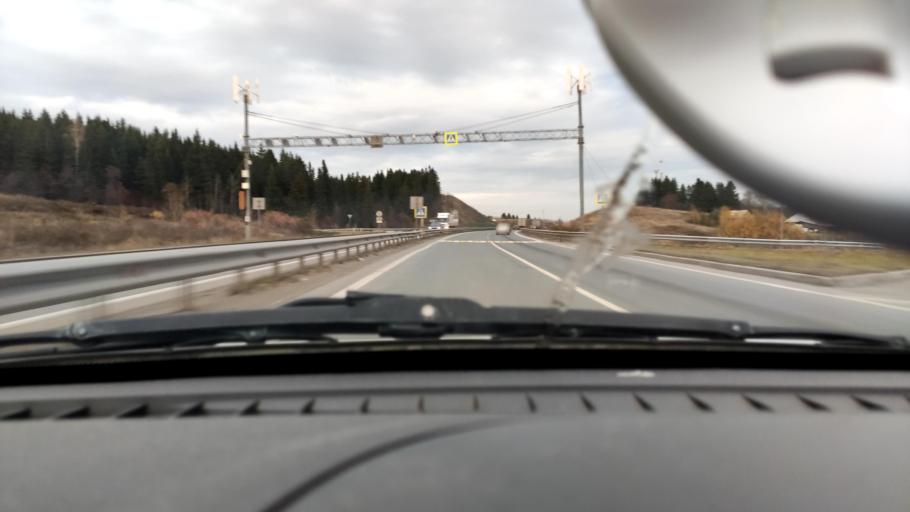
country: RU
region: Perm
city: Froly
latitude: 57.9347
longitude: 56.2134
